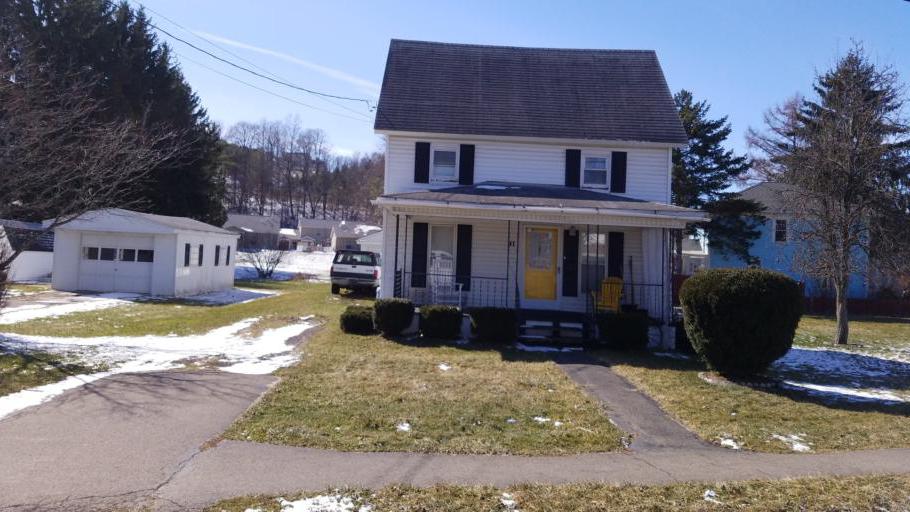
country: US
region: New York
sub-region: Allegany County
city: Wellsville
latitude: 42.1228
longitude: -77.9594
